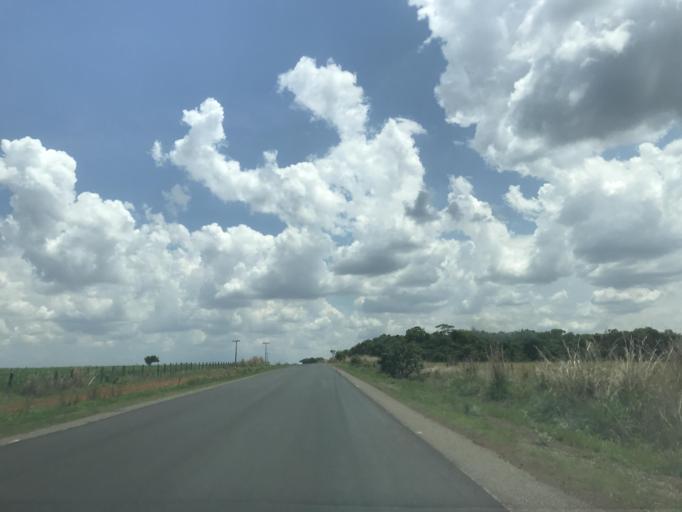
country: BR
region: Goias
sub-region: Piracanjuba
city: Piracanjuba
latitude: -17.3575
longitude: -48.7953
